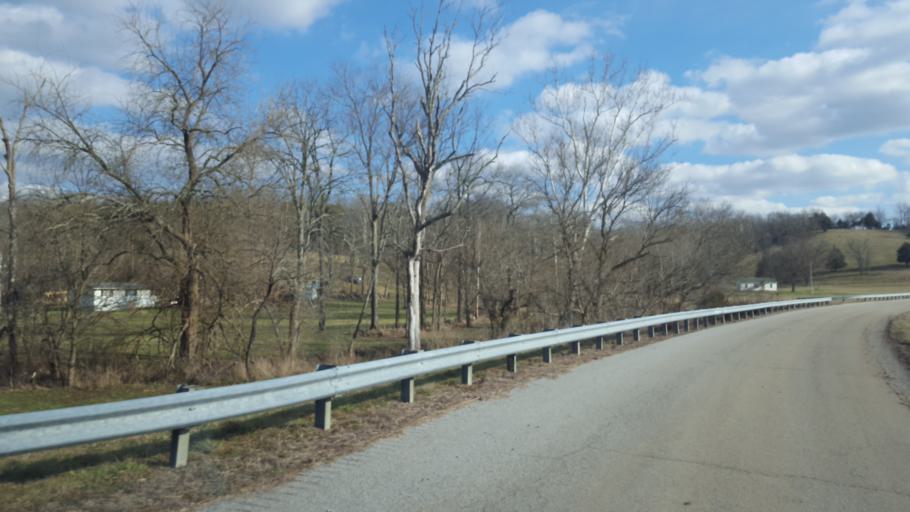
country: US
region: Kentucky
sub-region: Scott County
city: Georgetown
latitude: 38.3222
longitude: -84.5074
